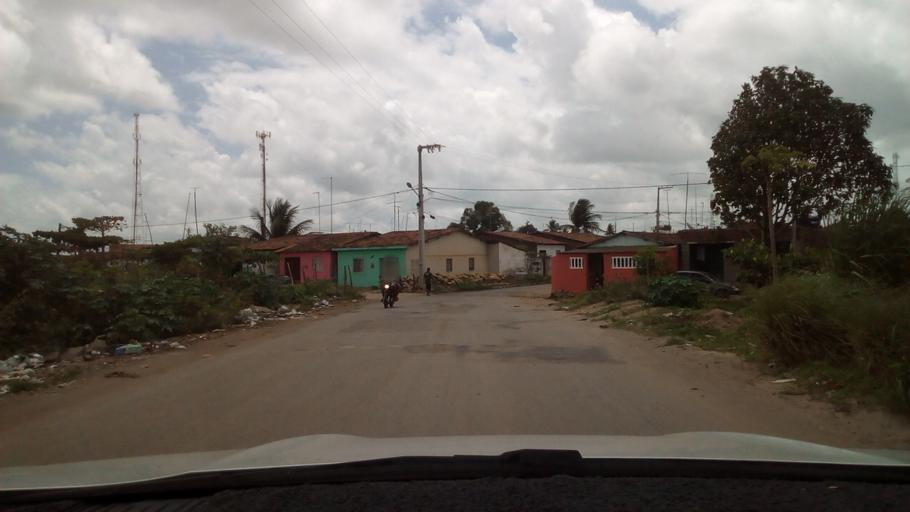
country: BR
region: Paraiba
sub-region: Caapora
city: Caapora
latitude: -7.5108
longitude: -34.9169
